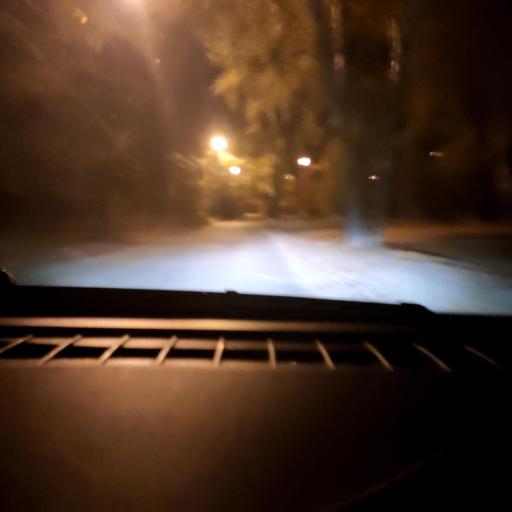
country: RU
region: Voronezj
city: Podgornoye
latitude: 51.7563
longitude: 39.1828
